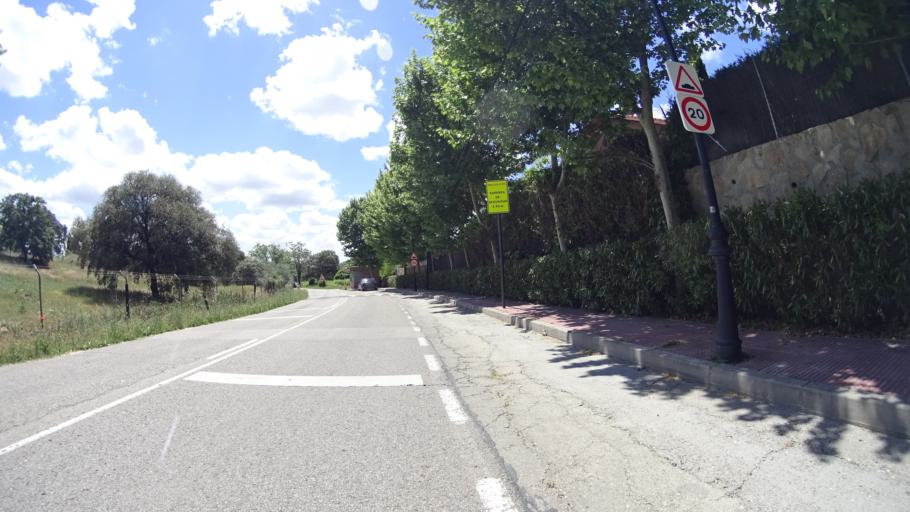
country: ES
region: Madrid
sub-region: Provincia de Madrid
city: Villanueva del Pardillo
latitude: 40.4631
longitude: -3.9461
